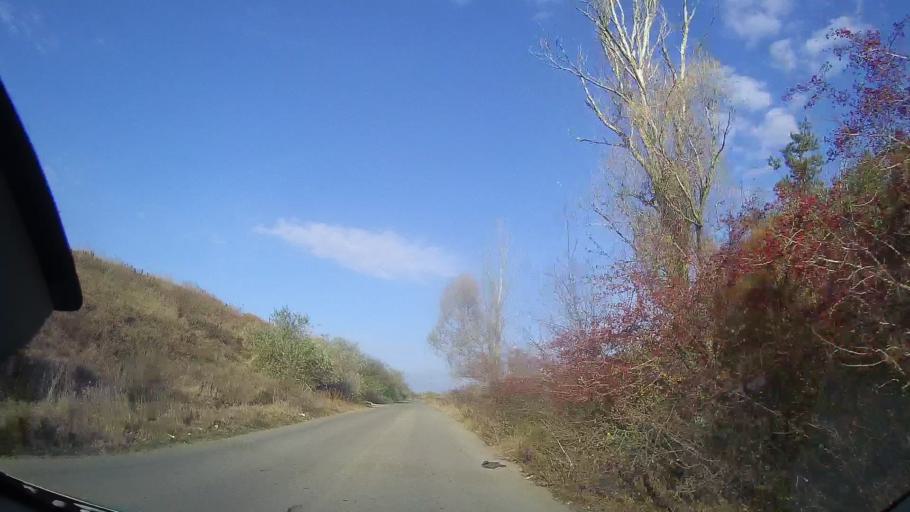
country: RO
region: Constanta
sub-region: Comuna Limanu
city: Limanu
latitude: 43.8207
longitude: 28.5210
